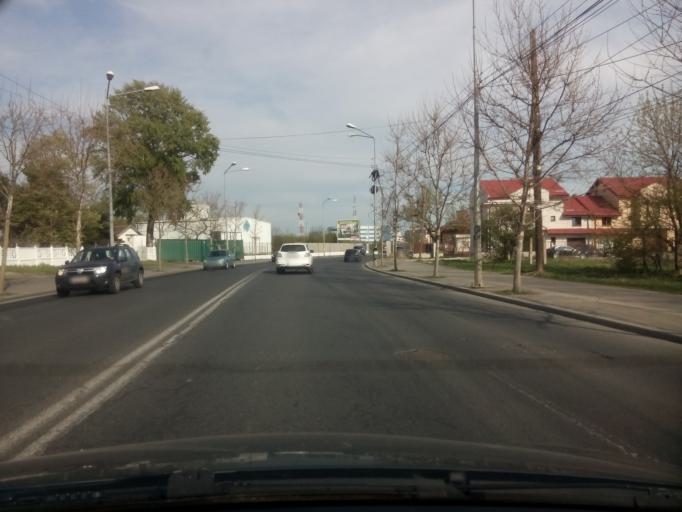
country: RO
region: Ilfov
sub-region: Comuna Otopeni
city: Otopeni
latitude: 44.5019
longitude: 26.0601
